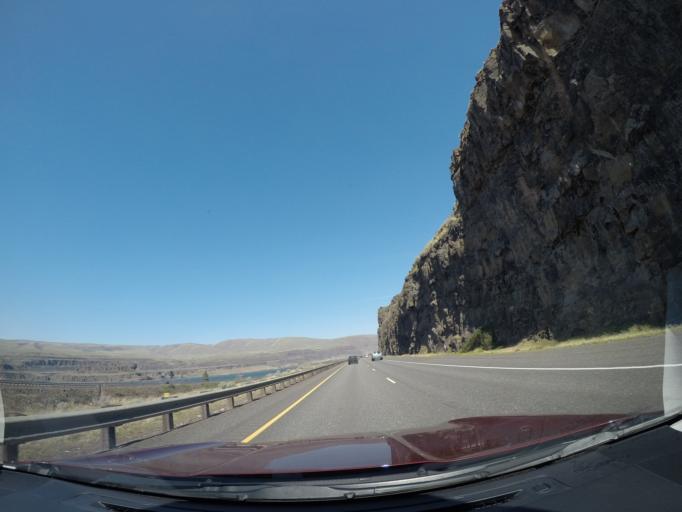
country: US
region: Washington
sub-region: Klickitat County
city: Dallesport
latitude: 45.6332
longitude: -121.0979
